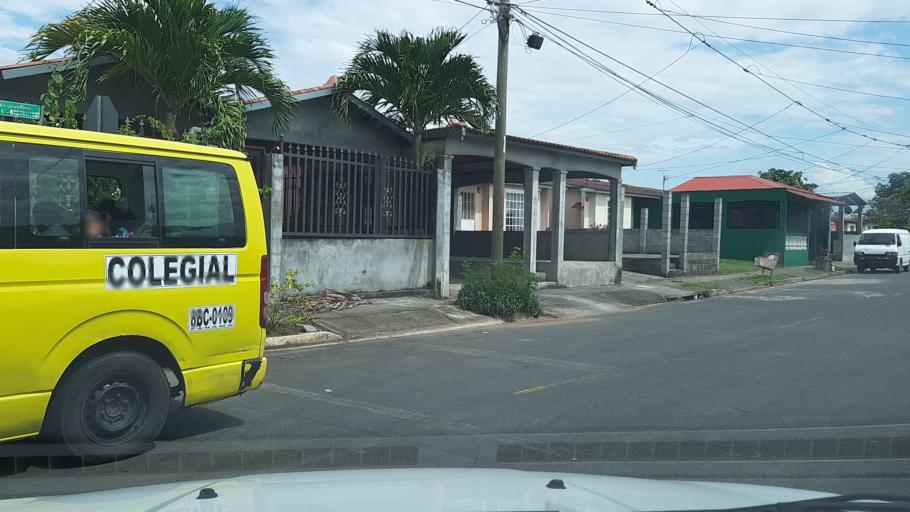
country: PA
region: Panama
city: Tocumen
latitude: 9.0728
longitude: -79.3616
